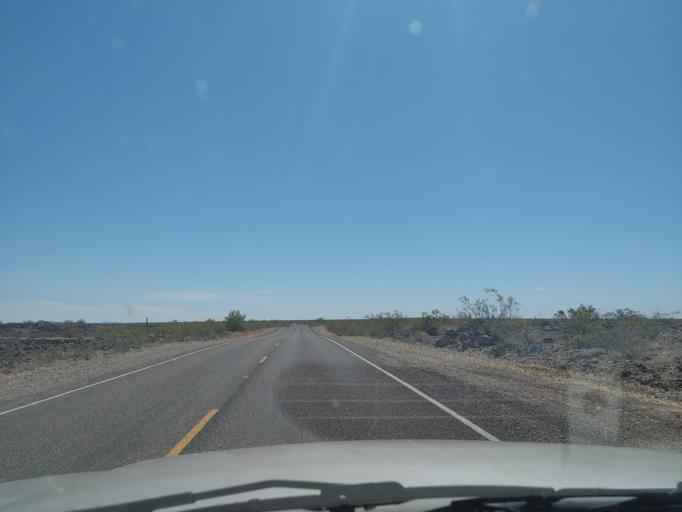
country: US
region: Arizona
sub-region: Maricopa County
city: Gila Bend
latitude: 32.9211
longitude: -113.2861
